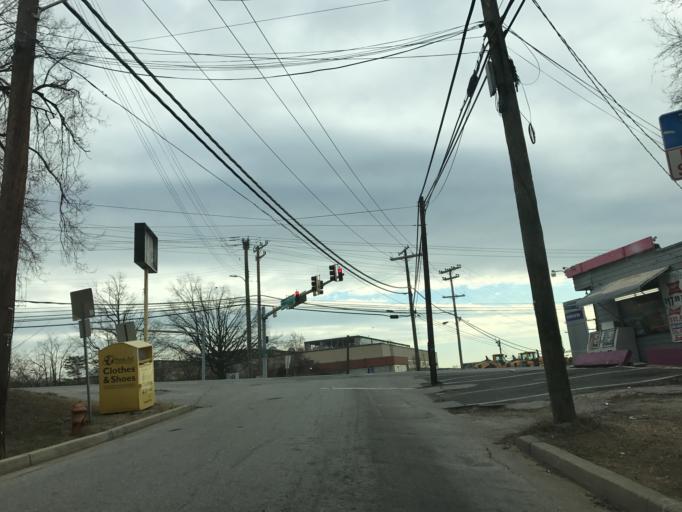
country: US
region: Maryland
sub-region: Baltimore County
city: Arbutus
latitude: 39.2349
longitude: -76.6876
